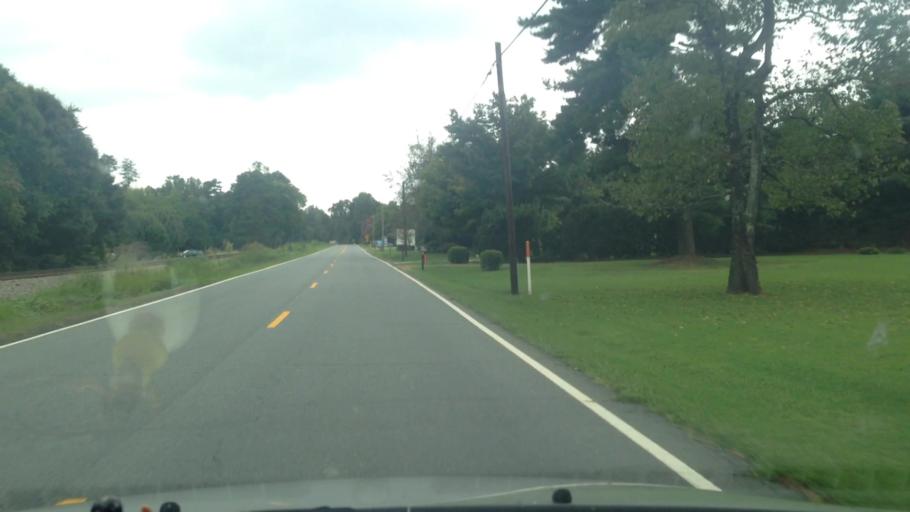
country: US
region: North Carolina
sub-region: Forsyth County
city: Walkertown
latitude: 36.2294
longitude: -80.1662
